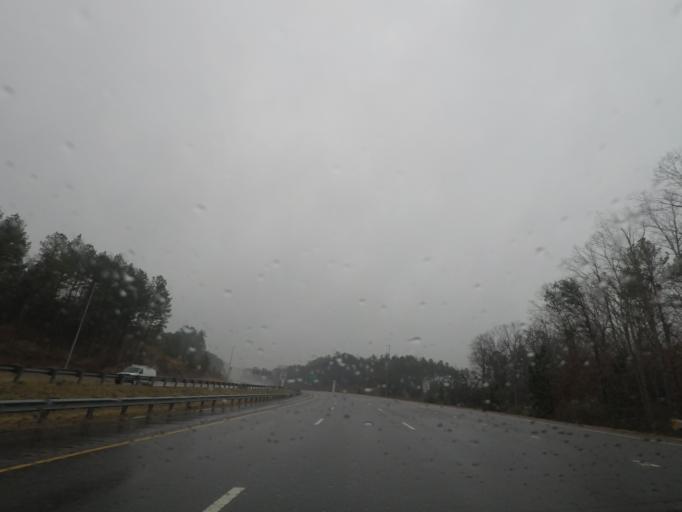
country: US
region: North Carolina
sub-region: Wake County
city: Morrisville
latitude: 35.8969
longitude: -78.8763
